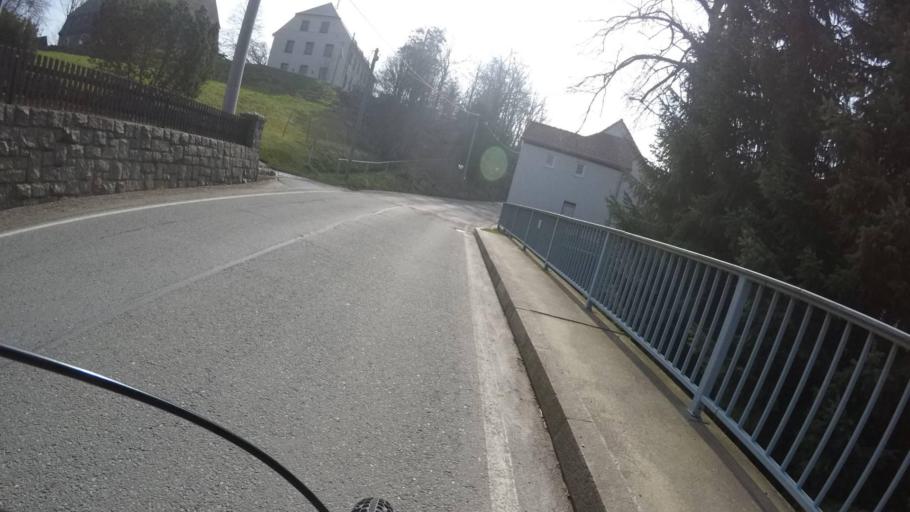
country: DE
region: Saxony
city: Niederfrohna
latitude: 50.8916
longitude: 12.6819
